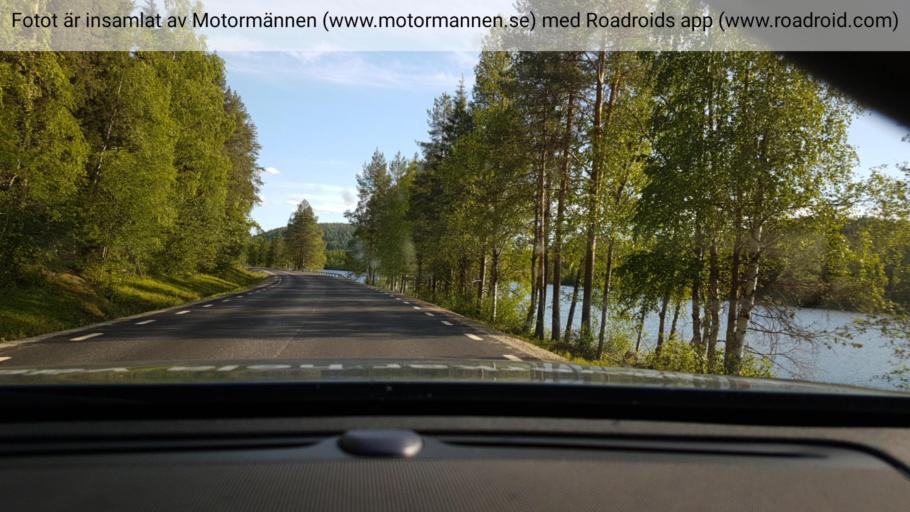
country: SE
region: Vaesterbotten
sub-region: Vindelns Kommun
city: Vindeln
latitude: 64.4477
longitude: 19.3392
